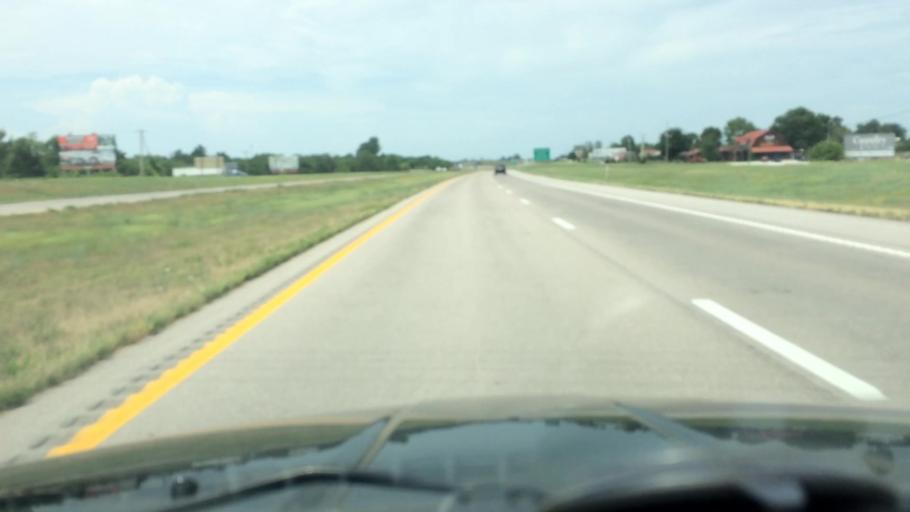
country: US
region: Missouri
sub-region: Polk County
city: Bolivar
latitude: 37.5643
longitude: -93.3934
